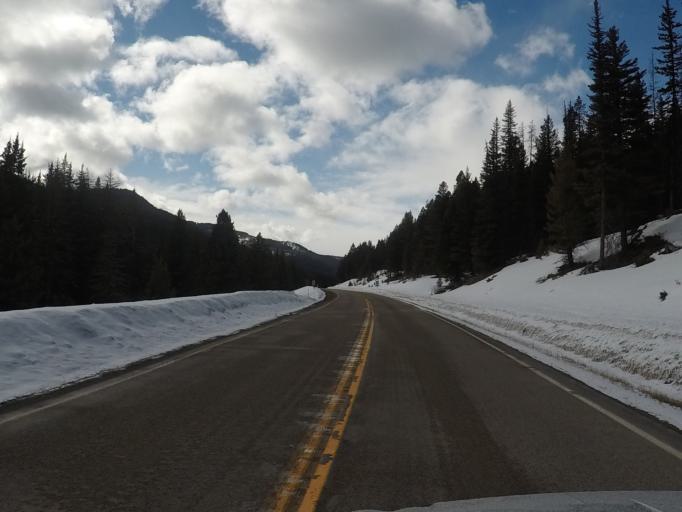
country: US
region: Montana
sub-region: Meagher County
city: White Sulphur Springs
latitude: 46.7604
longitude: -110.7258
